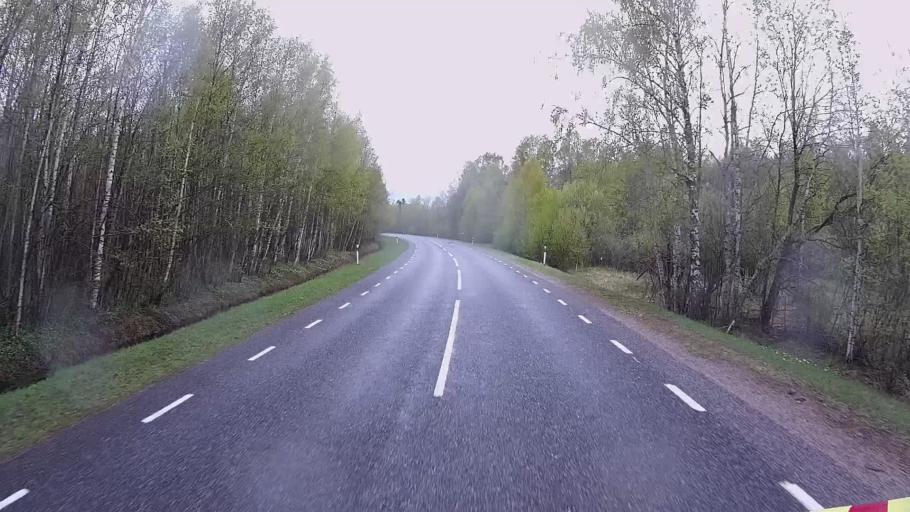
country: EE
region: Hiiumaa
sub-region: Kaerdla linn
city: Kardla
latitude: 58.7366
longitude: 22.5433
